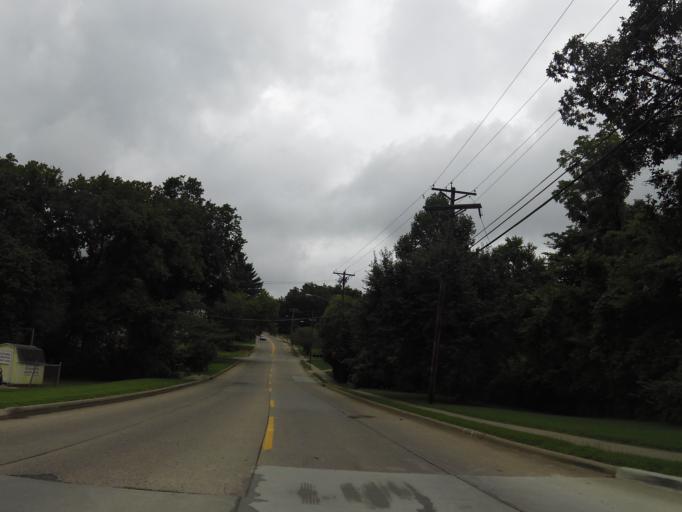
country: US
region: Missouri
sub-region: Cape Girardeau County
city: Cape Girardeau
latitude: 37.3330
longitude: -89.5464
